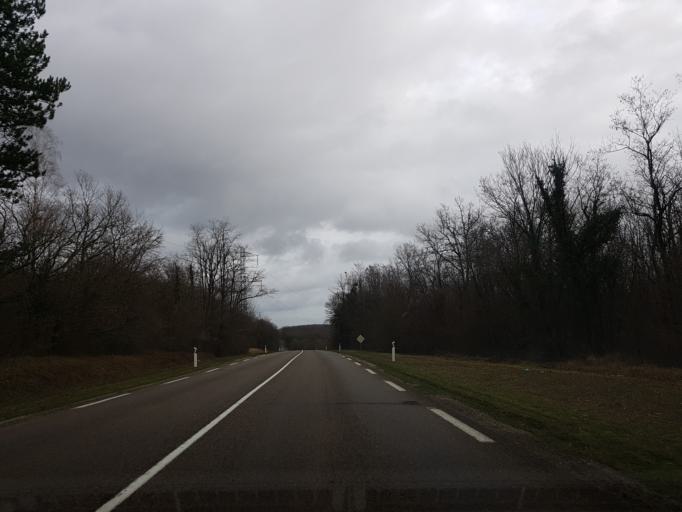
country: FR
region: Franche-Comte
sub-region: Departement de la Haute-Saone
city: Scey-sur-Saone-et-Saint-Albin
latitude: 47.6963
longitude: 5.9634
